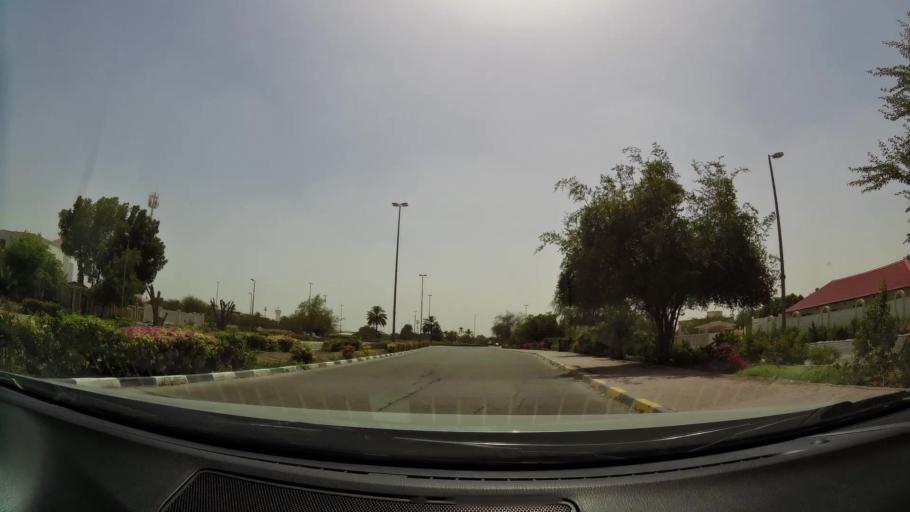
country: AE
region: Abu Dhabi
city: Al Ain
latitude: 24.2339
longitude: 55.7084
